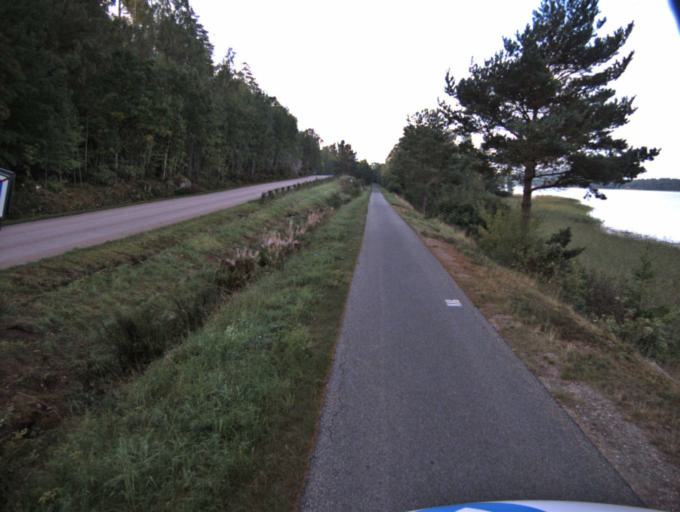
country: SE
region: Vaestra Goetaland
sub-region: Ulricehamns Kommun
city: Ulricehamn
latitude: 57.7504
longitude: 13.3941
